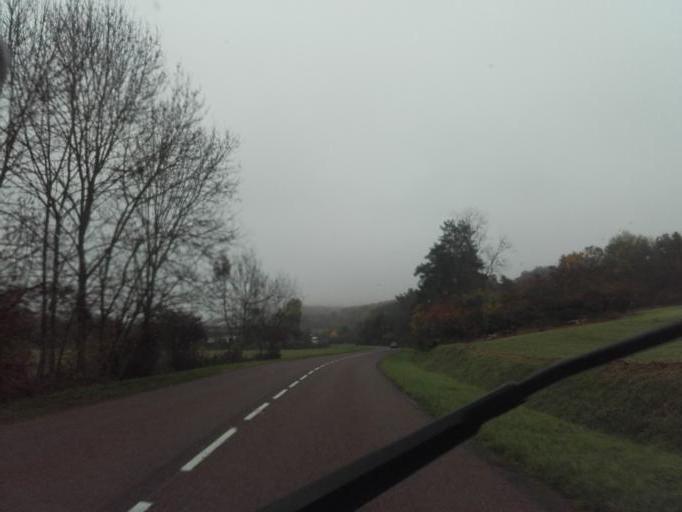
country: FR
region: Bourgogne
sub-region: Departement de la Cote-d'Or
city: Nuits-Saint-Georges
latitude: 47.1417
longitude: 4.8973
